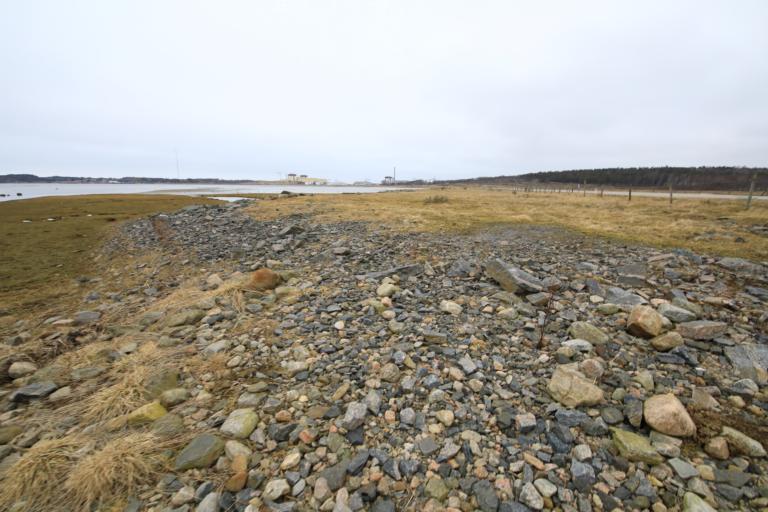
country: SE
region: Halland
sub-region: Kungsbacka Kommun
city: Frillesas
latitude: 57.2471
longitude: 12.1312
